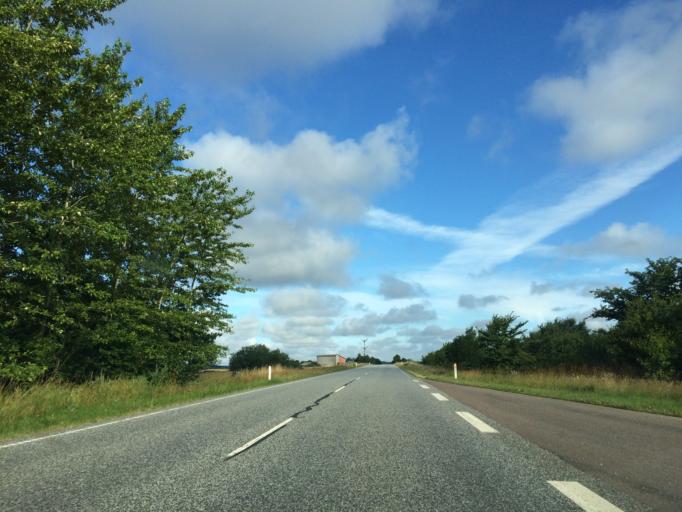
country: DK
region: Central Jutland
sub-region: Viborg Kommune
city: Bjerringbro
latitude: 56.3279
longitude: 9.5540
